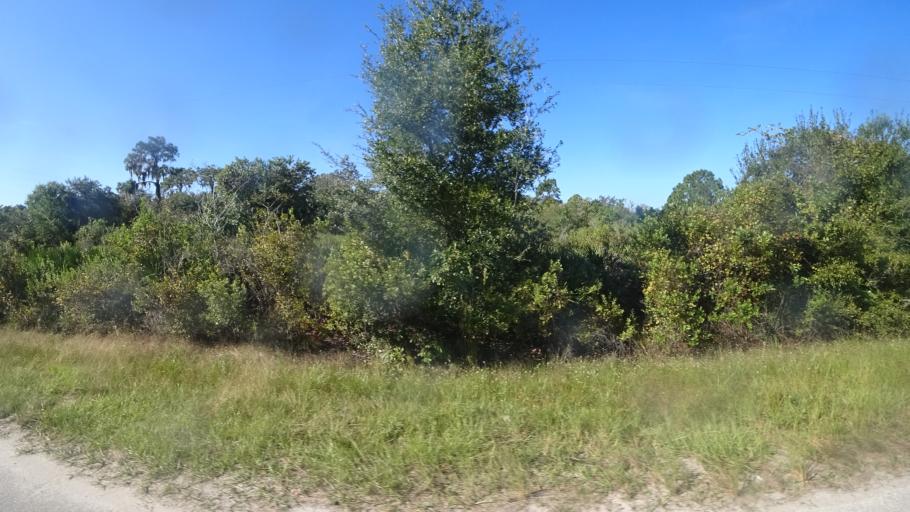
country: US
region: Florida
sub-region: Hillsborough County
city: Sun City Center
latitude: 27.6473
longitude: -82.3524
